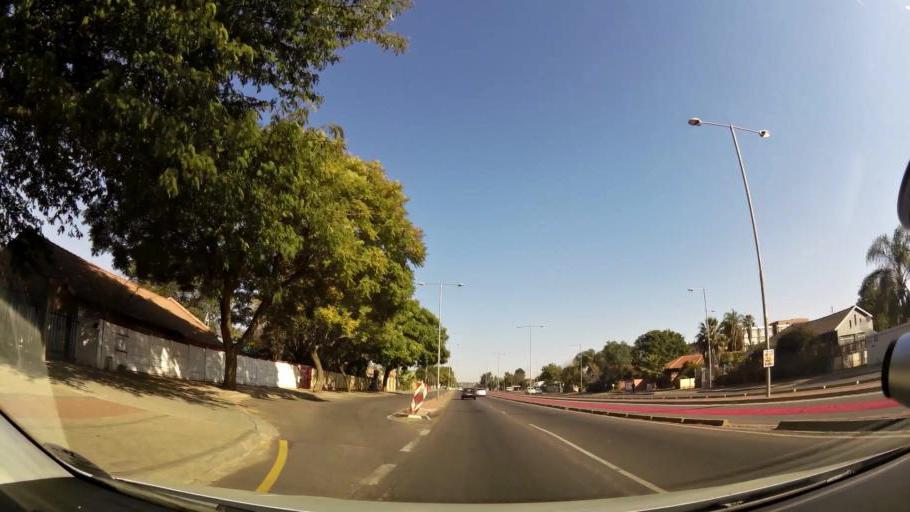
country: ZA
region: Gauteng
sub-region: City of Tshwane Metropolitan Municipality
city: Pretoria
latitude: -25.7015
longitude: 28.1876
